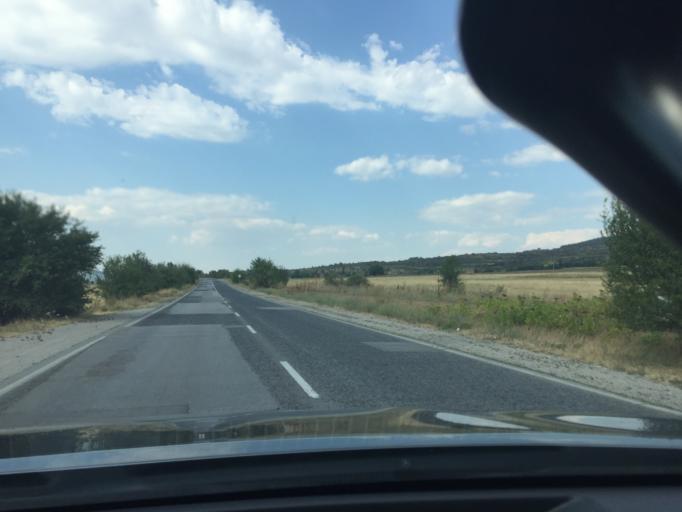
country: BG
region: Kyustendil
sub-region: Obshtina Boboshevo
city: Boboshevo
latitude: 42.1249
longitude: 23.0393
